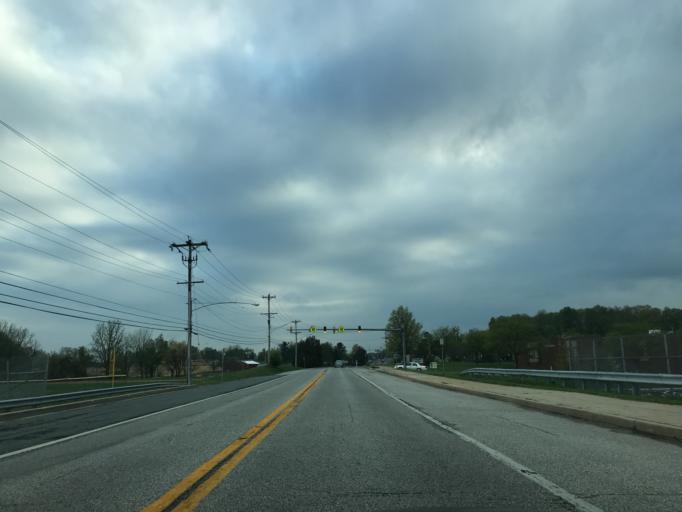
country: US
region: Pennsylvania
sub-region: York County
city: Susquehanna Trails
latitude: 39.6756
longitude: -76.4036
